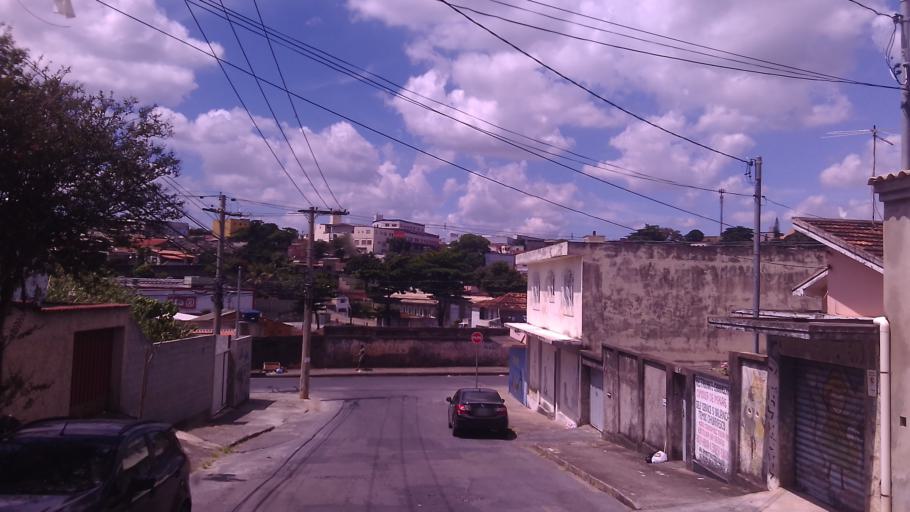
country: BR
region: Minas Gerais
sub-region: Contagem
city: Contagem
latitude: -19.9021
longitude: -44.0084
